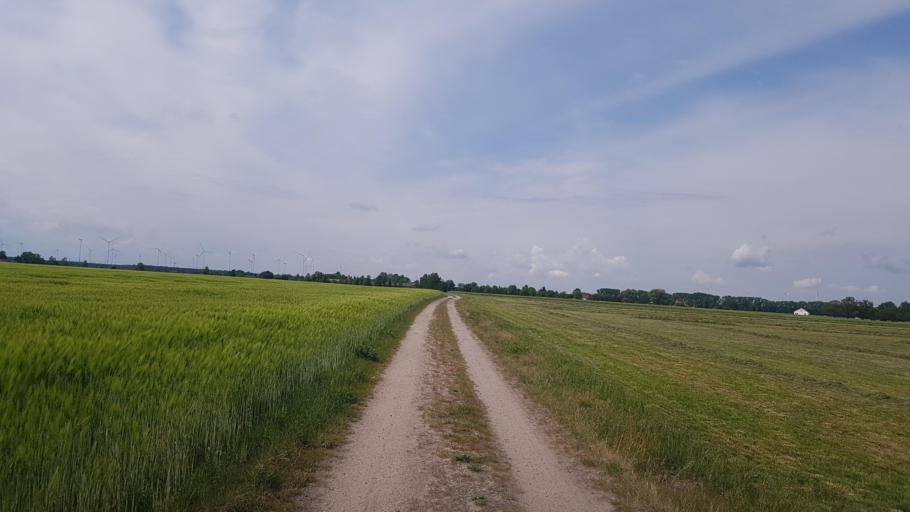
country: DE
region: Brandenburg
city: Sallgast
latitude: 51.5979
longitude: 13.8667
